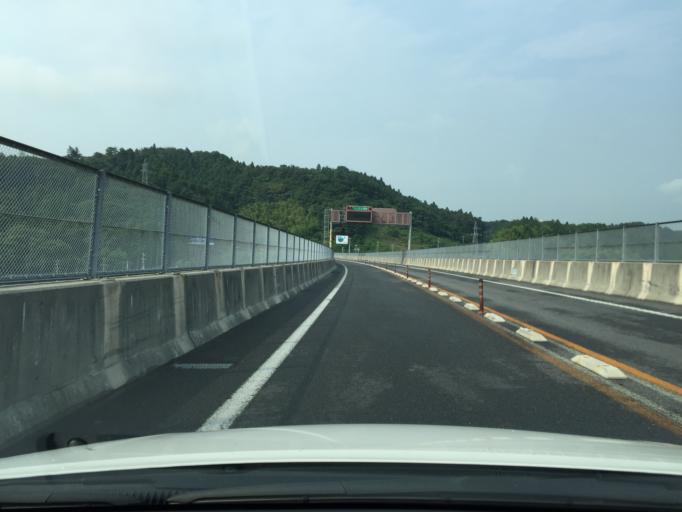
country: JP
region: Fukushima
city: Iwaki
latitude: 37.0694
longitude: 140.8399
